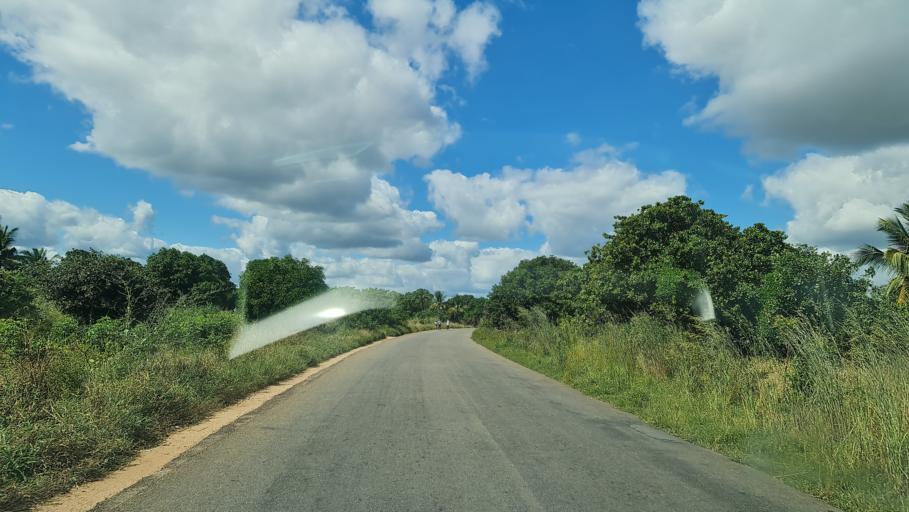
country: MZ
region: Zambezia
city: Quelimane
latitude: -17.5069
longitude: 36.2474
